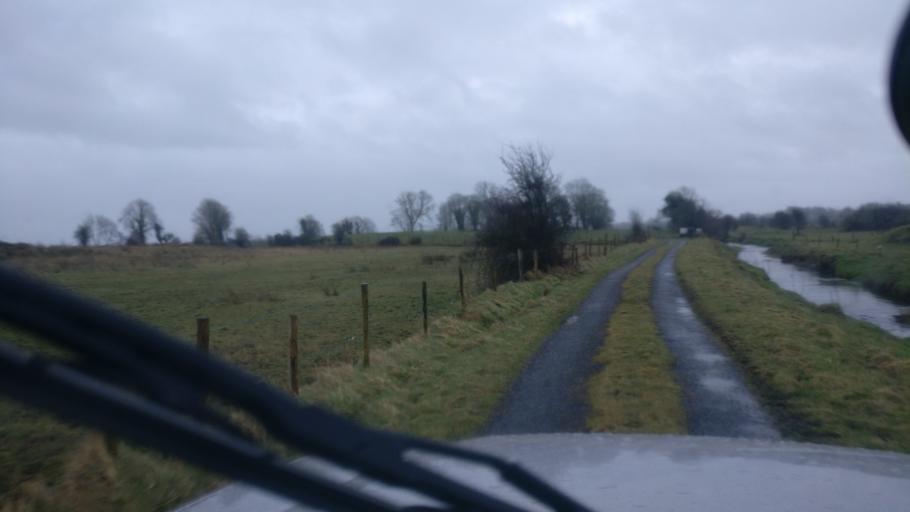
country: IE
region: Connaught
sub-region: County Galway
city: Ballinasloe
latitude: 53.2429
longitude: -8.3359
